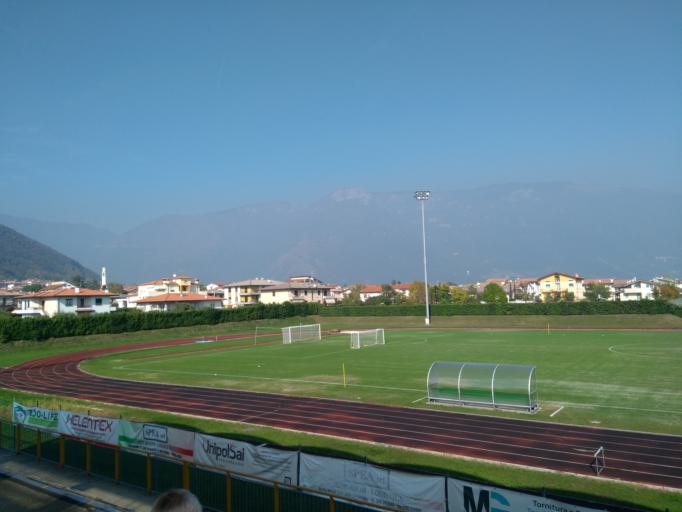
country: IT
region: Veneto
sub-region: Provincia di Vicenza
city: Piovene Rocchette
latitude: 45.7517
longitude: 11.4325
